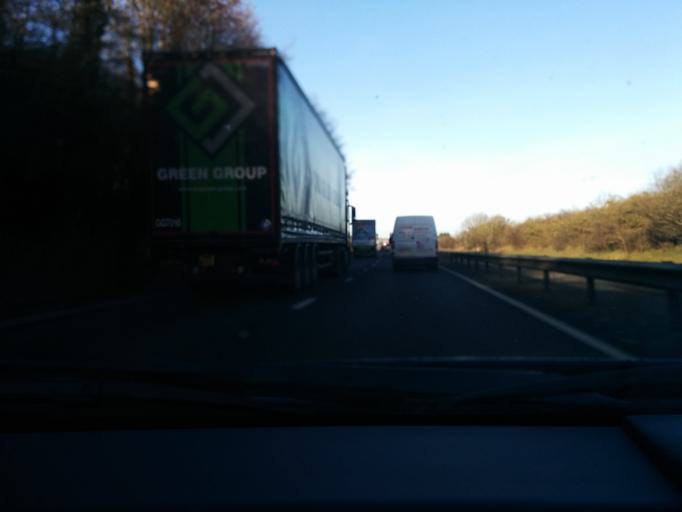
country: GB
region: England
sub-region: Oxfordshire
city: Oxford
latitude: 51.7283
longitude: -1.2596
